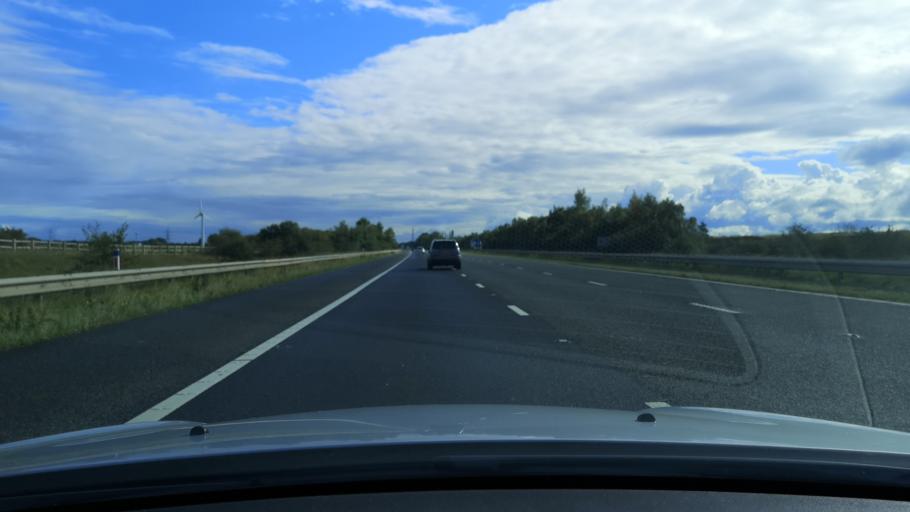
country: GB
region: England
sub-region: East Riding of Yorkshire
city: Pollington
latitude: 53.6844
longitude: -1.0806
